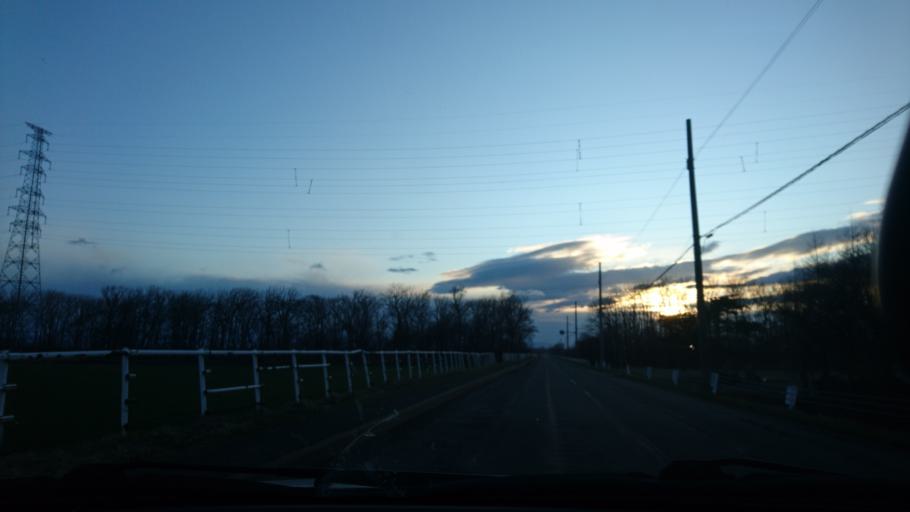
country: JP
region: Hokkaido
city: Ishikari
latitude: 43.1865
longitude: 141.4267
